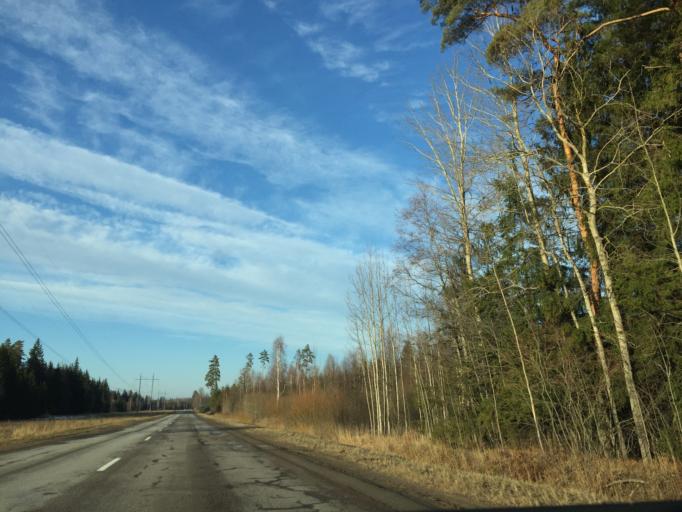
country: LV
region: Kekava
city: Balozi
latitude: 56.7905
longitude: 24.0759
